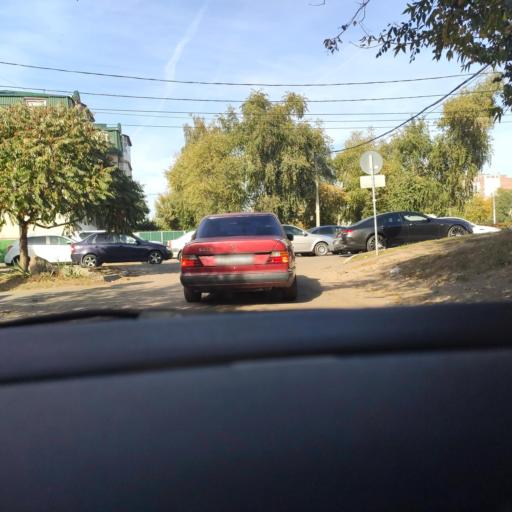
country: RU
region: Voronezj
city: Voronezh
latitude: 51.6949
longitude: 39.1817
